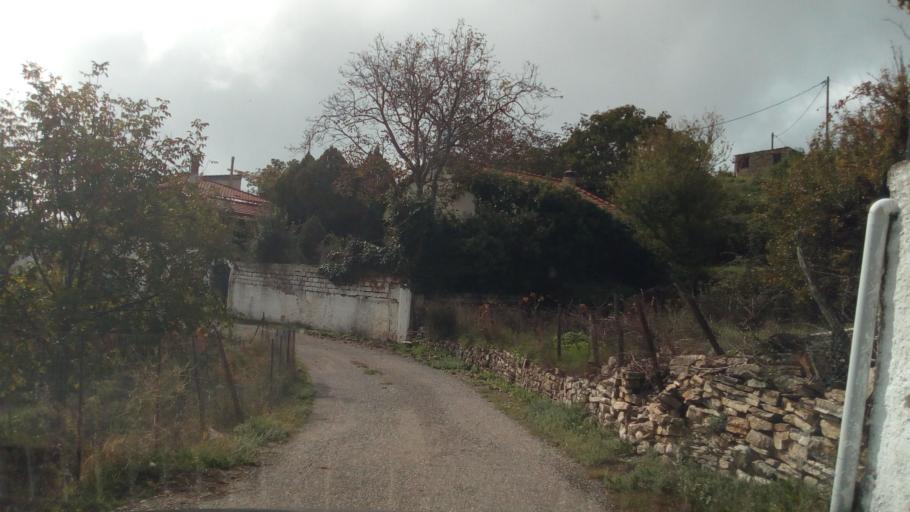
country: GR
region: West Greece
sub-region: Nomos Aitolias kai Akarnanias
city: Nafpaktos
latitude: 38.4510
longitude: 21.9686
